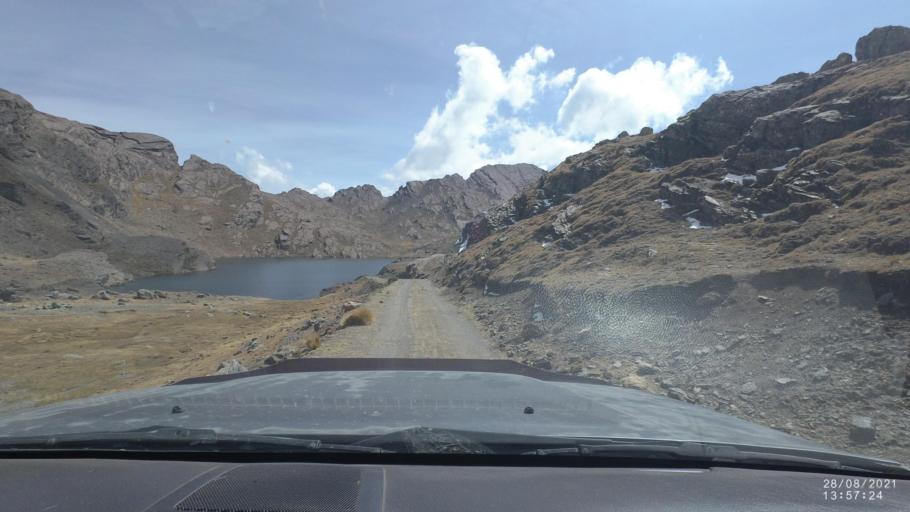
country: BO
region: Cochabamba
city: Sipe Sipe
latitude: -17.2757
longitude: -66.3852
